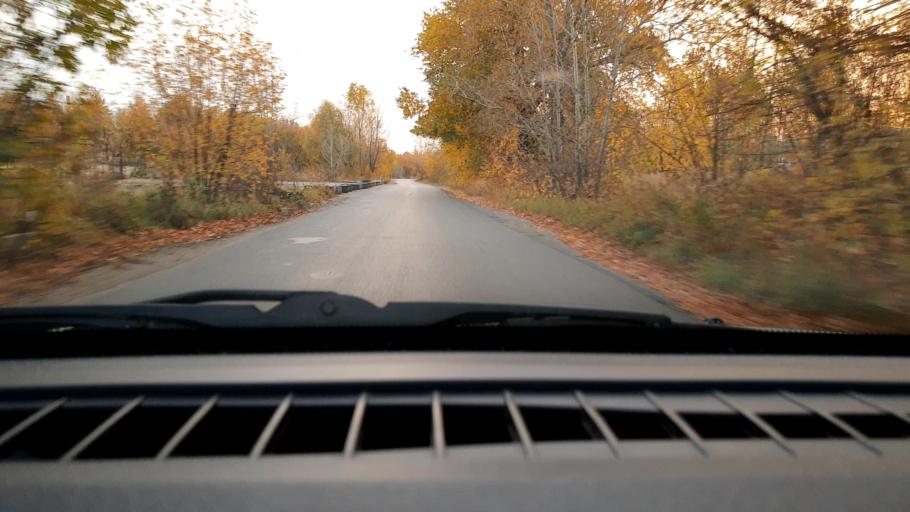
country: RU
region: Nizjnij Novgorod
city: Nizhniy Novgorod
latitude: 56.2351
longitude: 43.9065
